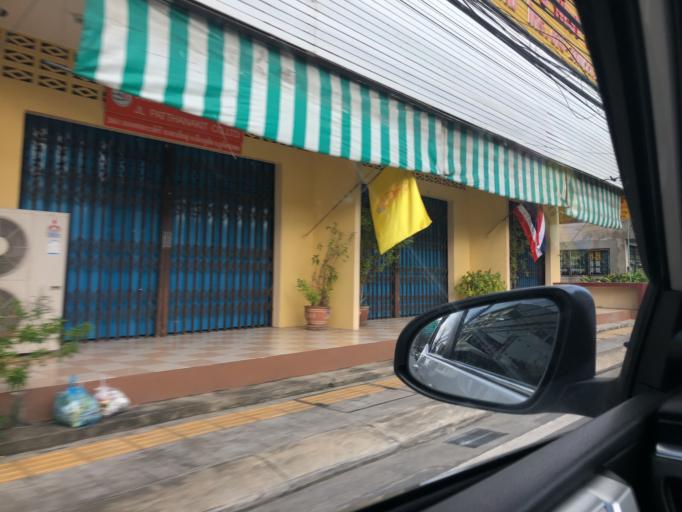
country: TH
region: Phuket
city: Wichit
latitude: 7.8958
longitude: 98.3894
